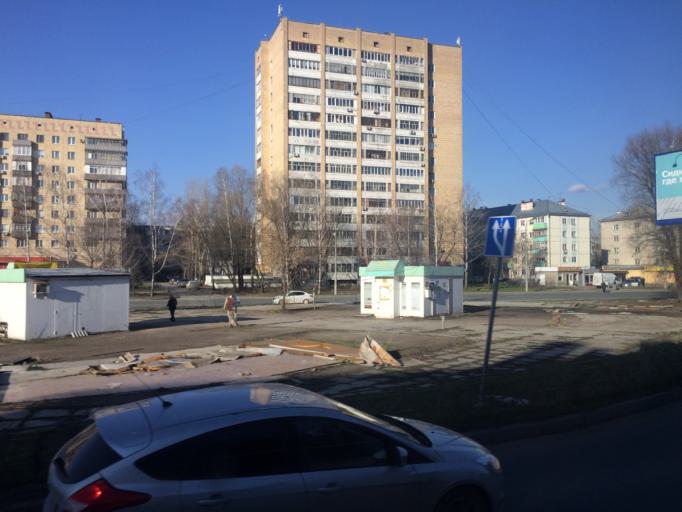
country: RU
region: Tatarstan
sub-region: Gorod Kazan'
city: Kazan
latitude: 55.8195
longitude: 49.0534
